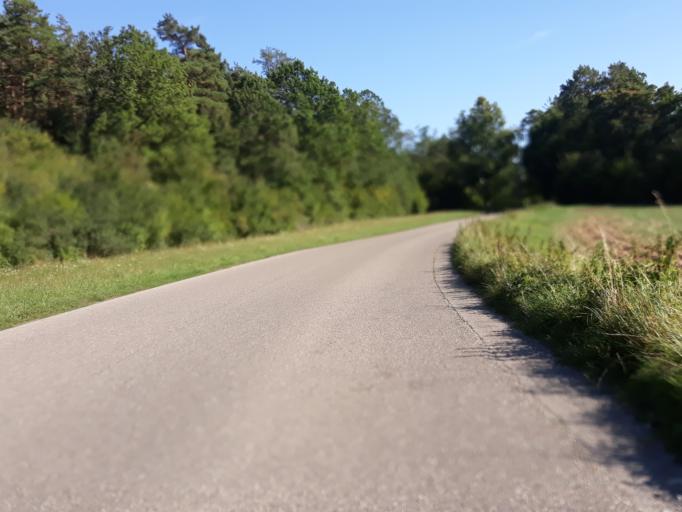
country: DE
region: Baden-Wuerttemberg
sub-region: Karlsruhe Region
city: Gechingen
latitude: 48.6881
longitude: 8.8420
